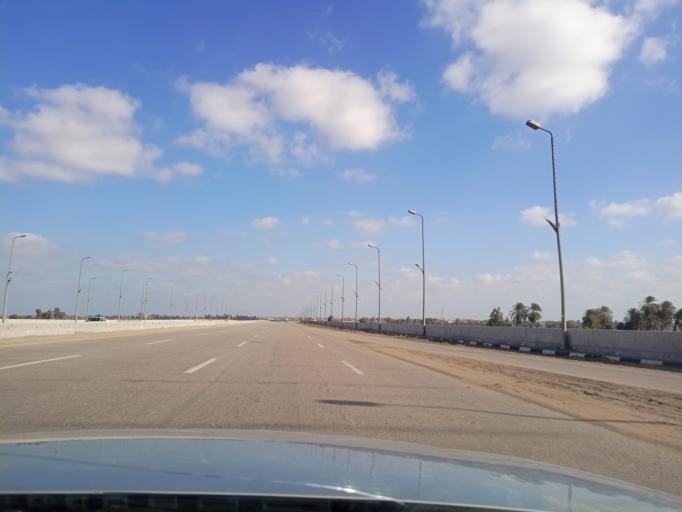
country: EG
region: Muhafazat al Minufiyah
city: Ashmun
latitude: 30.3246
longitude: 30.8319
